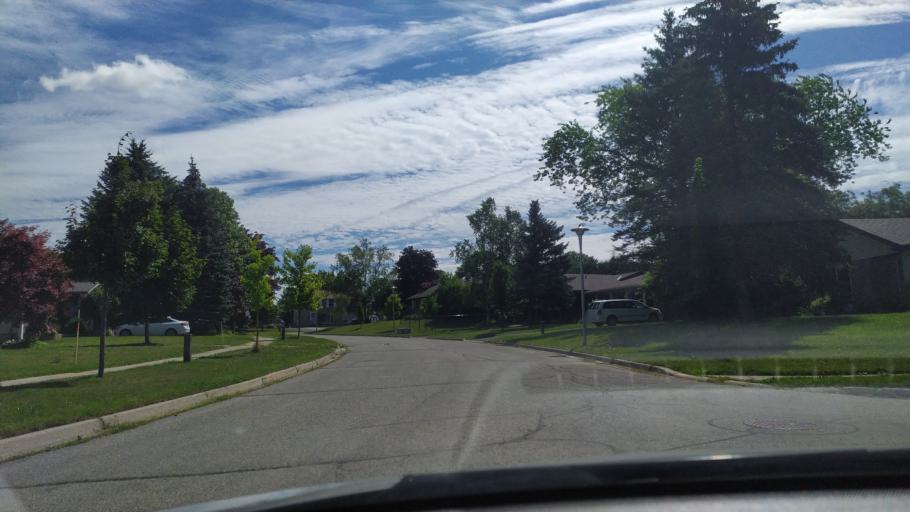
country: CA
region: Ontario
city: Stratford
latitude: 43.3742
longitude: -80.9448
